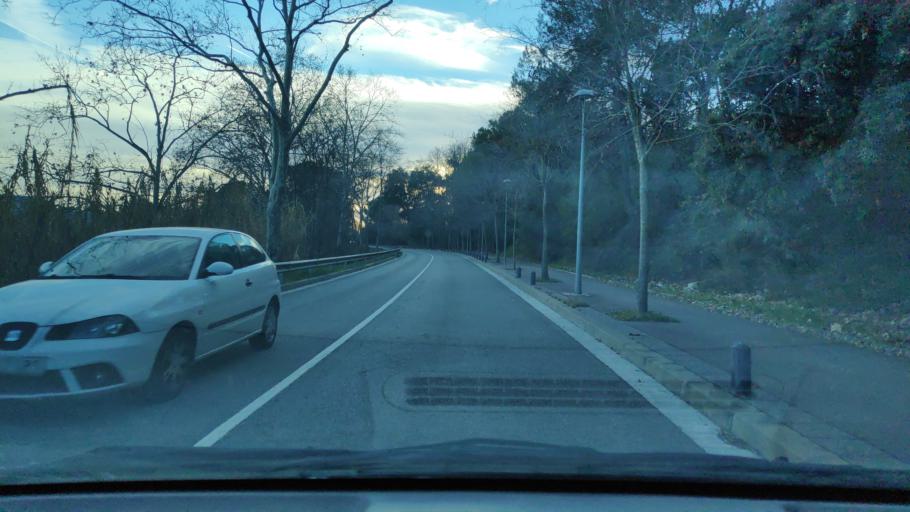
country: ES
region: Catalonia
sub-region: Provincia de Barcelona
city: Montmelo
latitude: 41.5656
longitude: 2.2609
